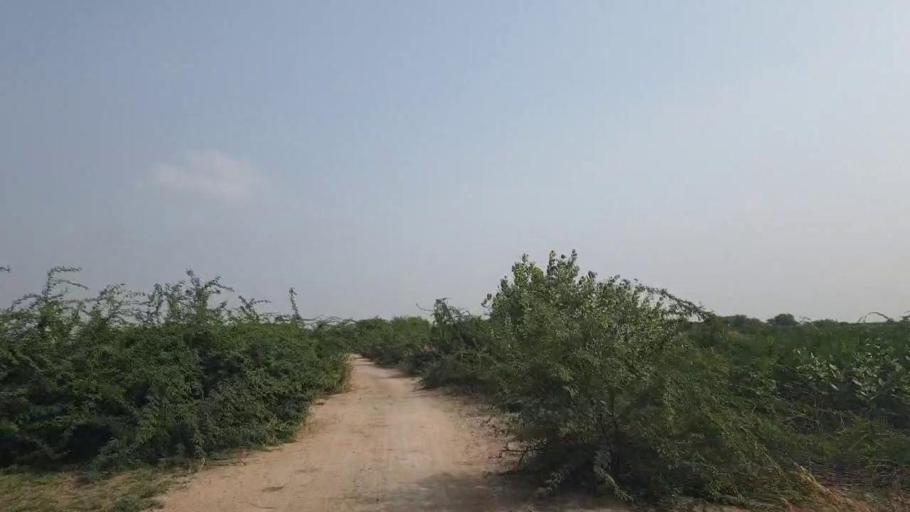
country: PK
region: Sindh
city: Badin
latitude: 24.5474
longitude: 68.6969
